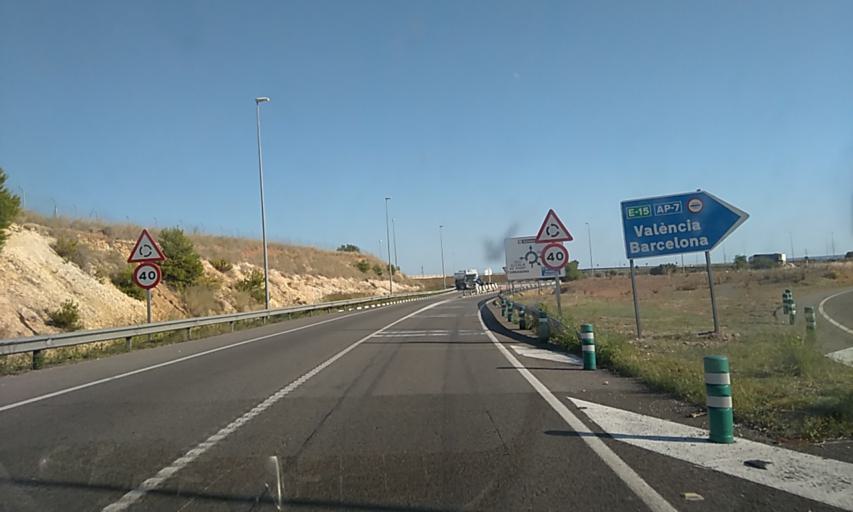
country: ES
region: Valencia
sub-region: Provincia de Castello
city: Torreblanca
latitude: 40.2297
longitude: 0.2119
